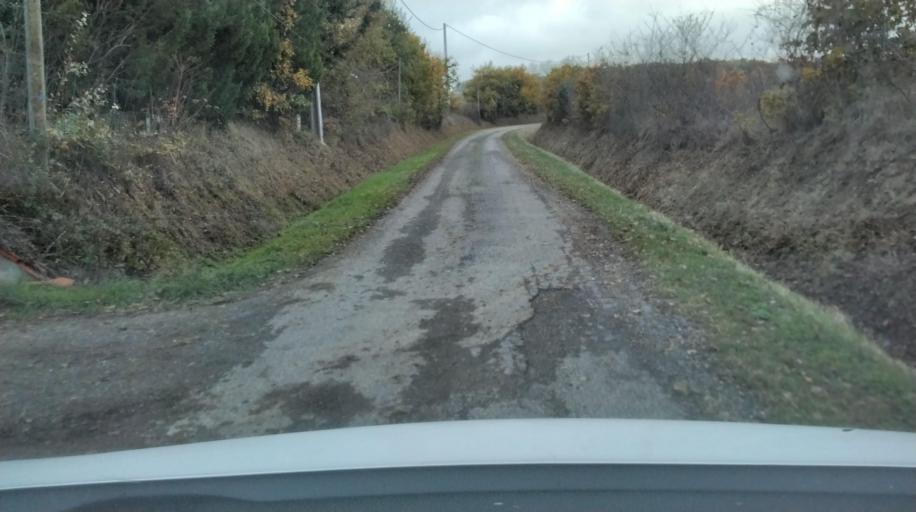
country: FR
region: Midi-Pyrenees
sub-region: Departement de la Haute-Garonne
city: Le Fousseret
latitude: 43.2716
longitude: 1.0299
